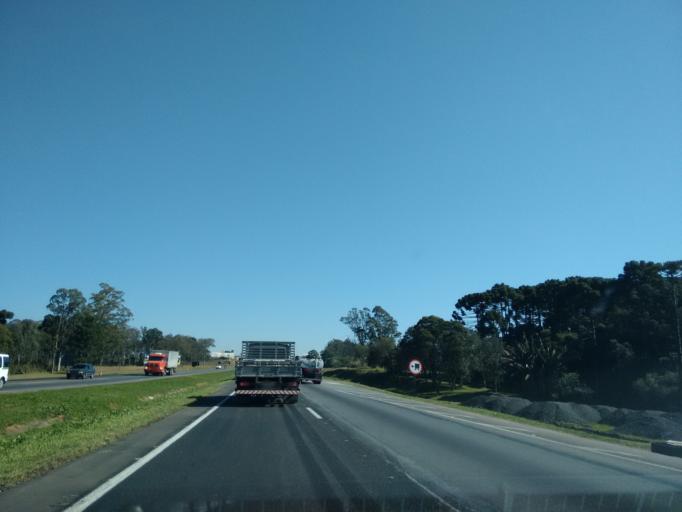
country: BR
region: Parana
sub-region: Sao Jose Dos Pinhais
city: Sao Jose dos Pinhais
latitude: -25.5632
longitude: -49.2557
